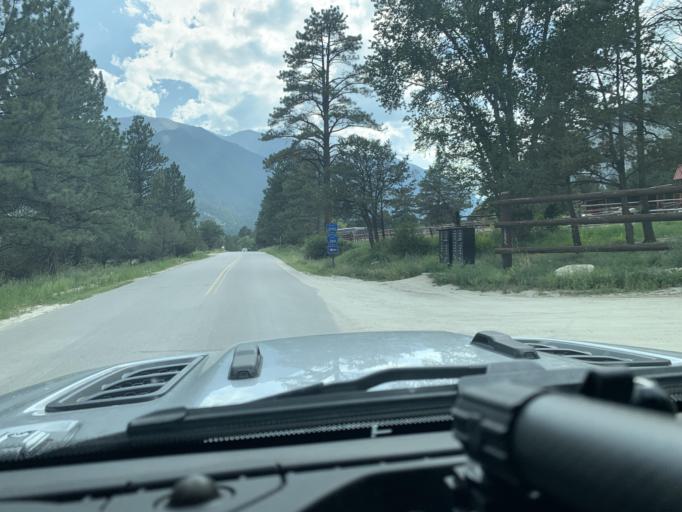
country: US
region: Colorado
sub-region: Chaffee County
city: Buena Vista
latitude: 38.7235
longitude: -106.1786
